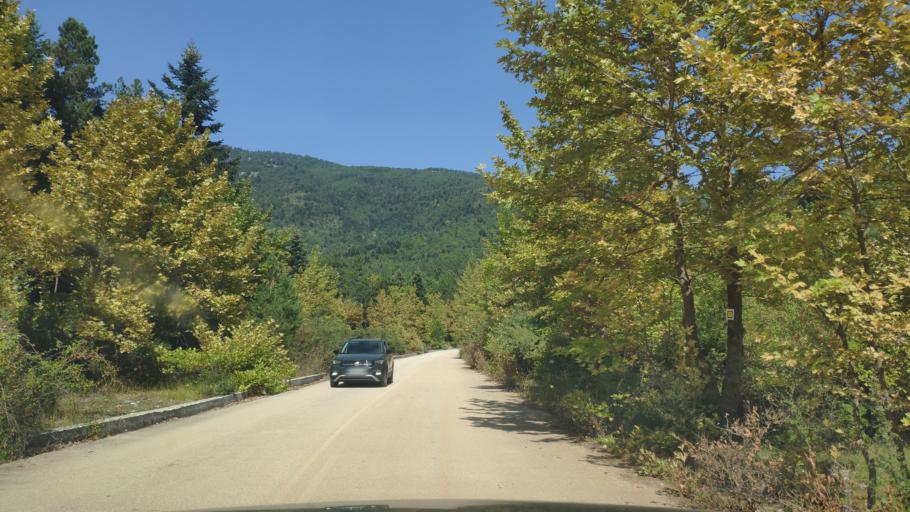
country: GR
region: West Greece
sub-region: Nomos Achaias
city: Kalavryta
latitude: 37.9283
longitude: 22.2792
